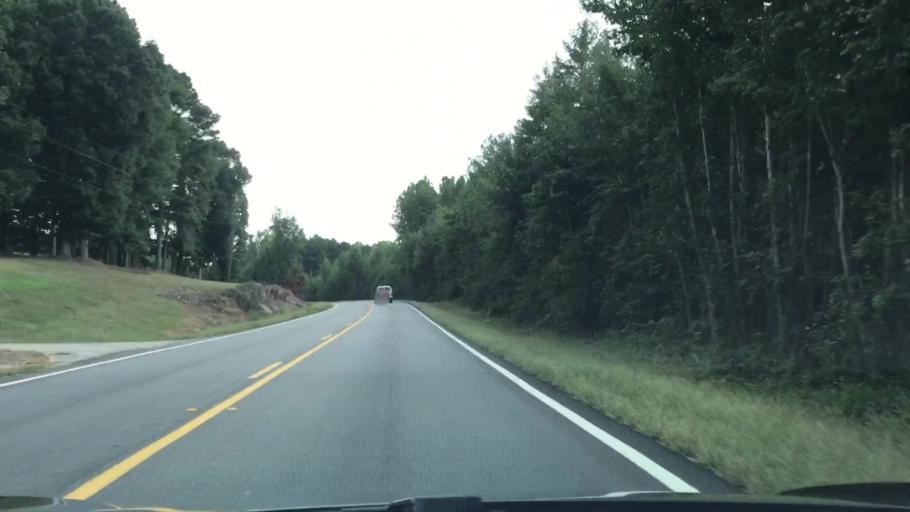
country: US
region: Georgia
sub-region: Greene County
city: Union Point
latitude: 33.5437
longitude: -83.0951
